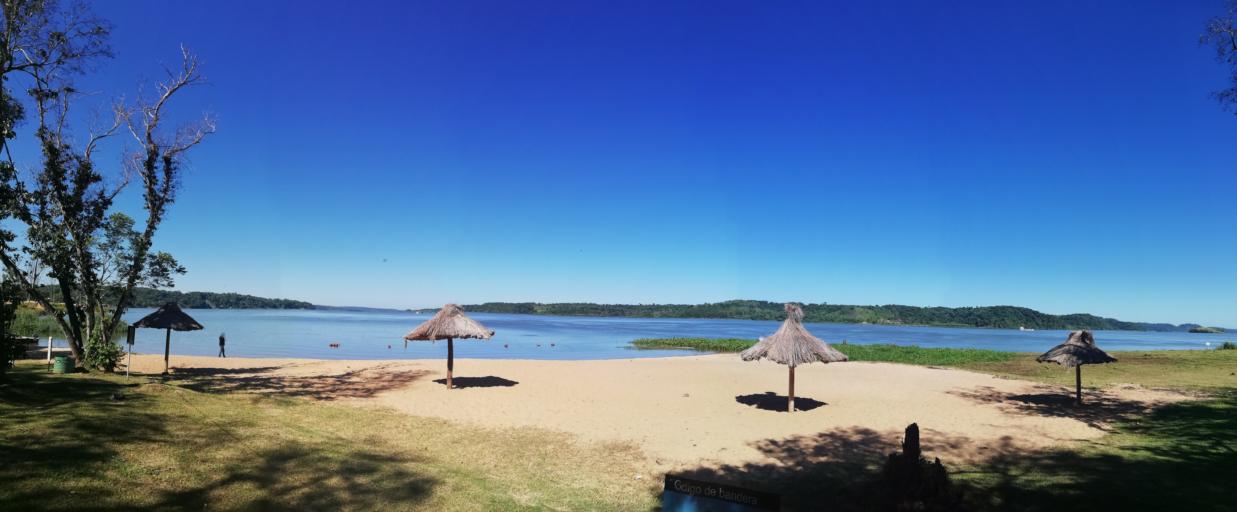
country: AR
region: Misiones
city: Santa Ana
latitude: -27.3308
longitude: -55.5872
